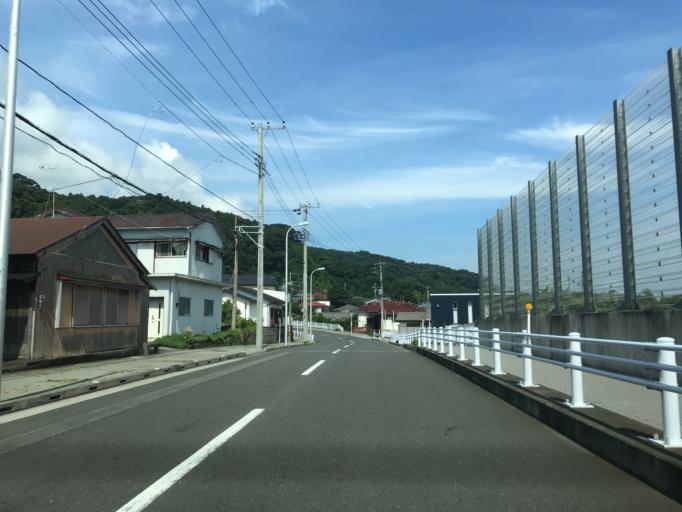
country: JP
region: Shizuoka
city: Ito
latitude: 34.7826
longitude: 139.4161
